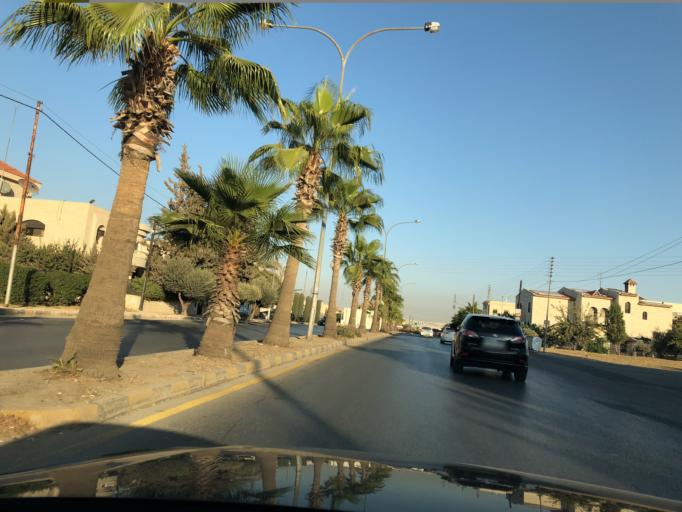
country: JO
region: Amman
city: Al Bunayyat ash Shamaliyah
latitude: 31.9429
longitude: 35.8787
